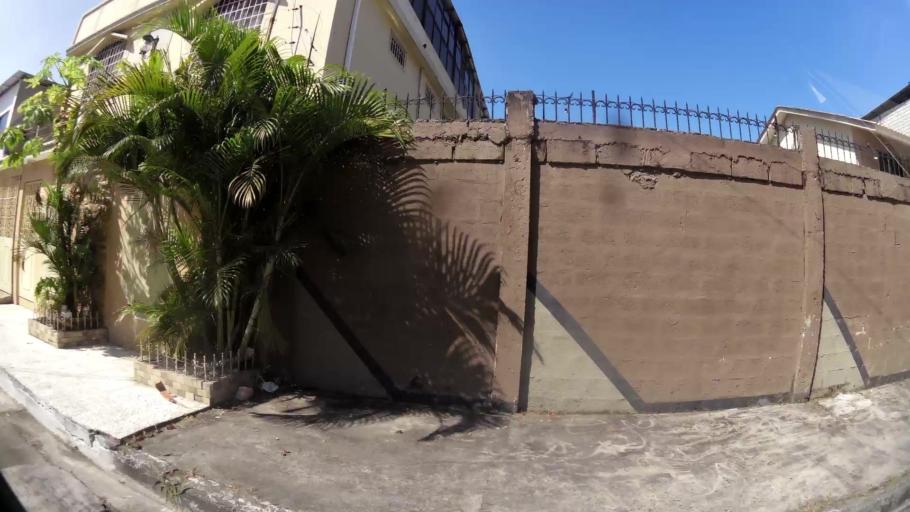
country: EC
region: Guayas
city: Guayaquil
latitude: -2.1877
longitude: -79.9159
